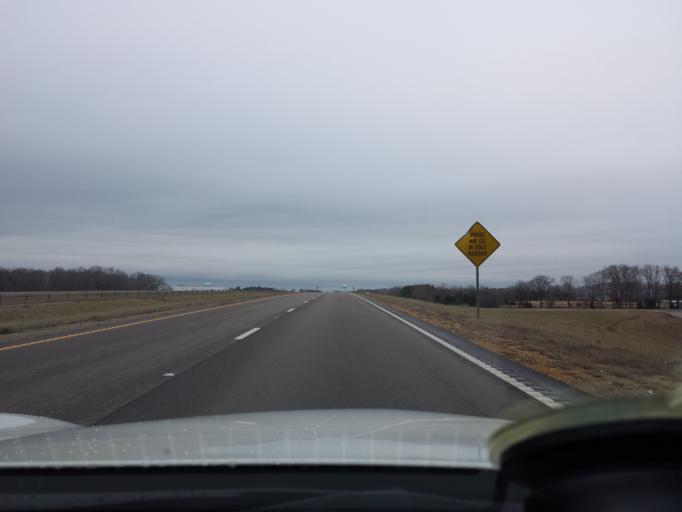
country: US
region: Mississippi
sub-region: Lee County
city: Shannon
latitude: 34.1514
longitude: -88.7023
